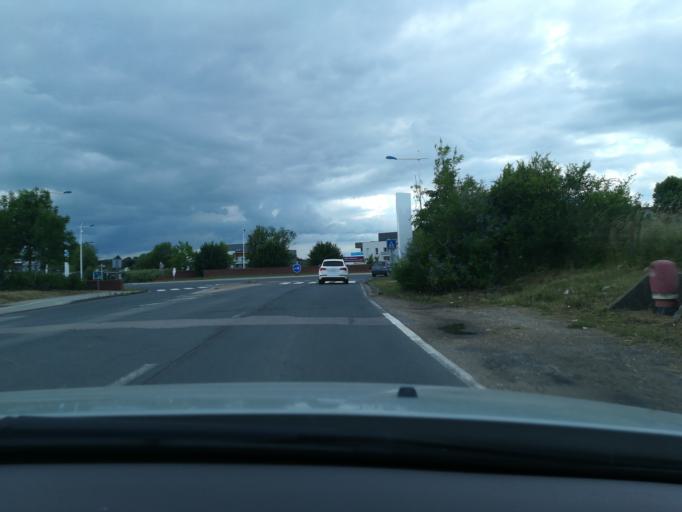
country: FR
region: Haute-Normandie
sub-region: Departement de la Seine-Maritime
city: Isneauville
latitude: 49.4913
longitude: 1.1450
